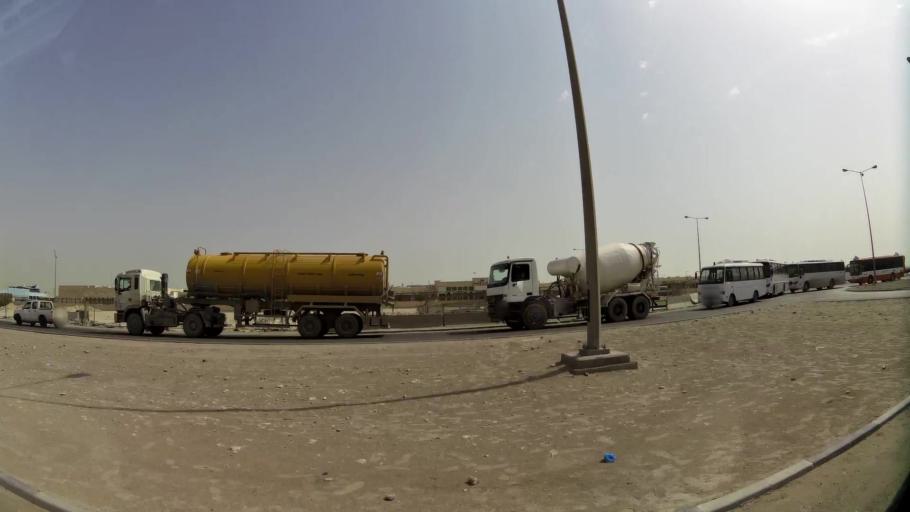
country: QA
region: Al Wakrah
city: Al Wukayr
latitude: 25.1849
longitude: 51.4605
